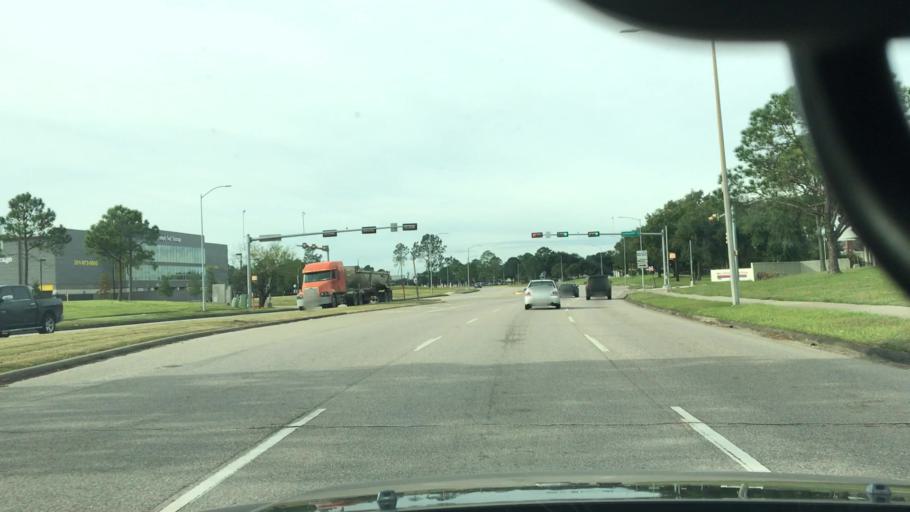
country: US
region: Texas
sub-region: Harris County
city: Webster
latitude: 29.5531
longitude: -95.1228
